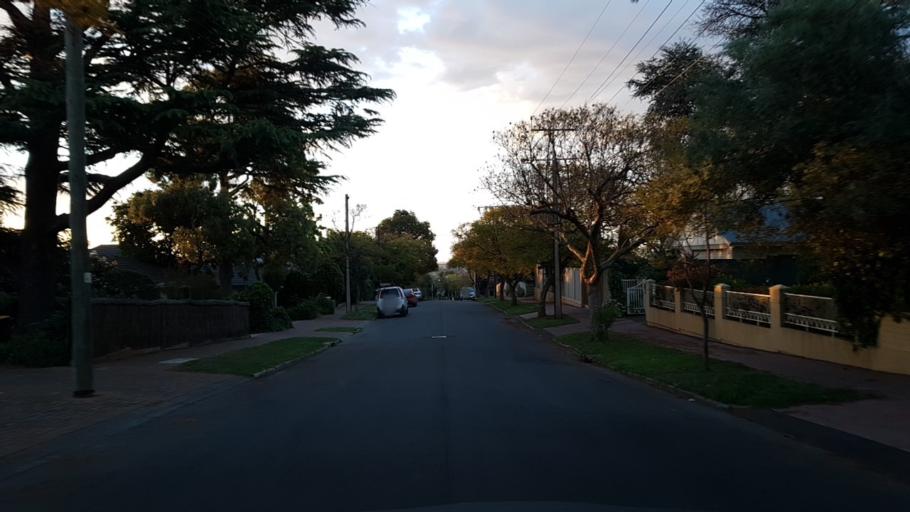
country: AU
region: South Australia
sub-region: Burnside
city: Linden Park
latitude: -34.9526
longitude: 138.6478
